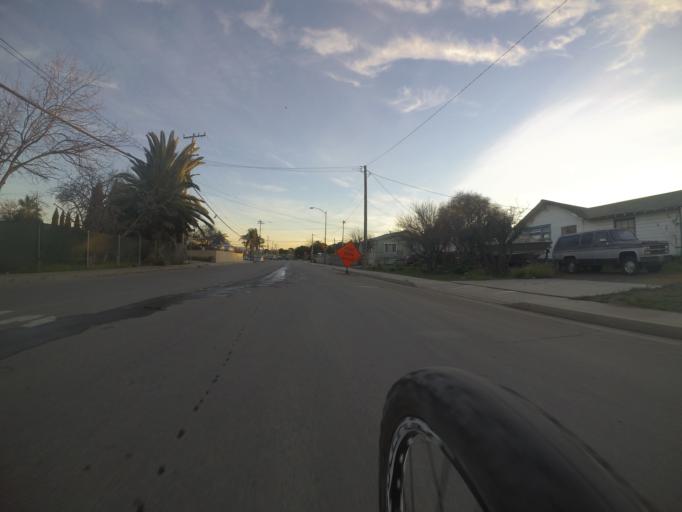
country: US
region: California
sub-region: Santa Clara County
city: Milpitas
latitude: 37.4270
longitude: -121.9748
